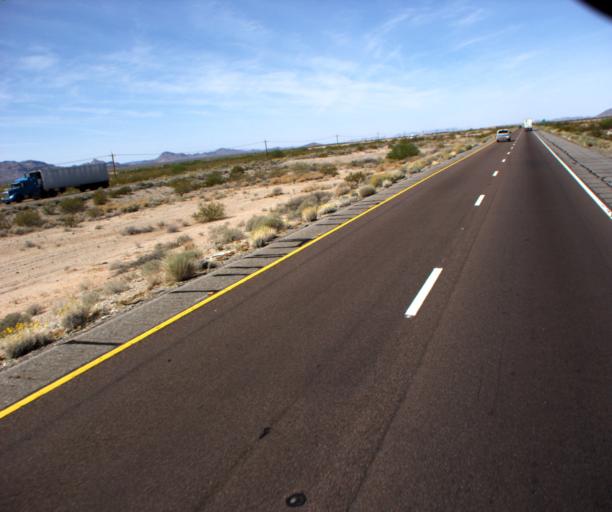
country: US
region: Arizona
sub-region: La Paz County
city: Salome
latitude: 33.5650
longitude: -113.3248
